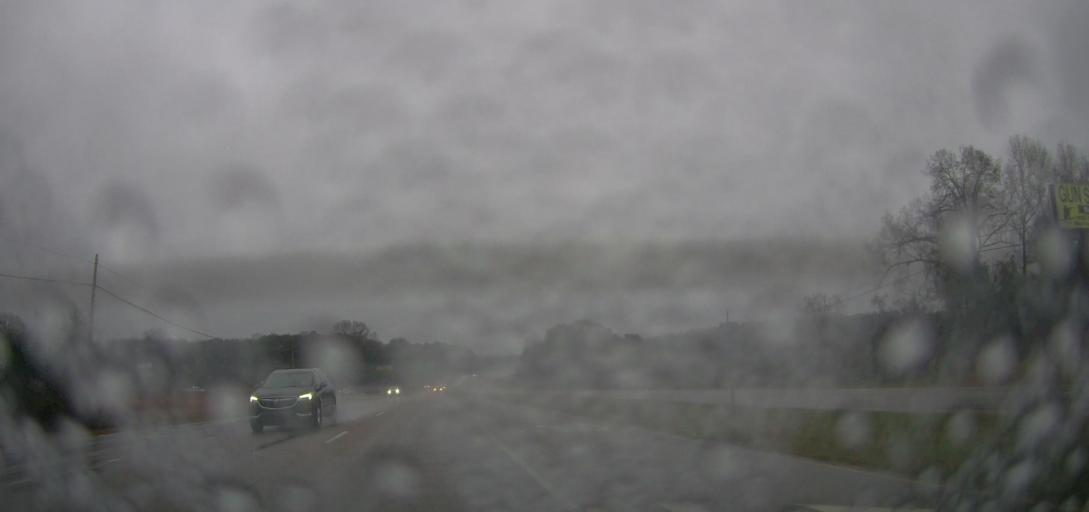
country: US
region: Alabama
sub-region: Autauga County
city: Prattville
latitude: 32.4339
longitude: -86.4197
